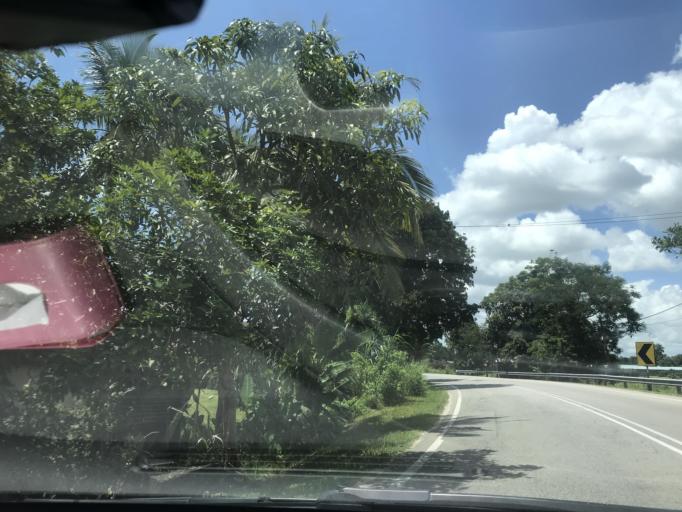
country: MY
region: Kelantan
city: Tumpat
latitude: 6.1973
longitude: 102.1321
